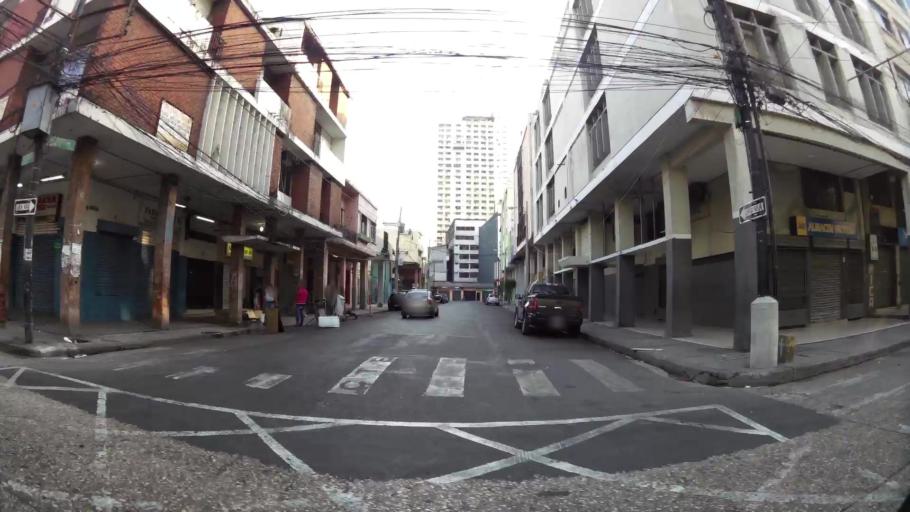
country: EC
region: Guayas
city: Guayaquil
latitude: -2.1931
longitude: -79.8888
